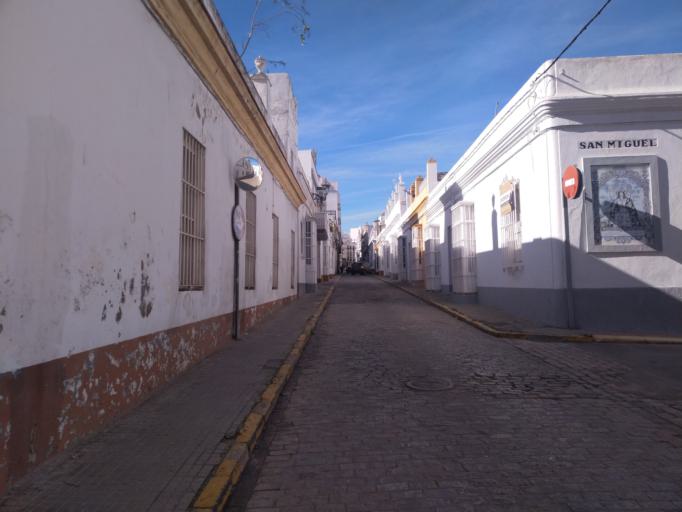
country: ES
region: Andalusia
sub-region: Provincia de Cadiz
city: San Fernando
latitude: 36.4700
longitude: -6.1942
